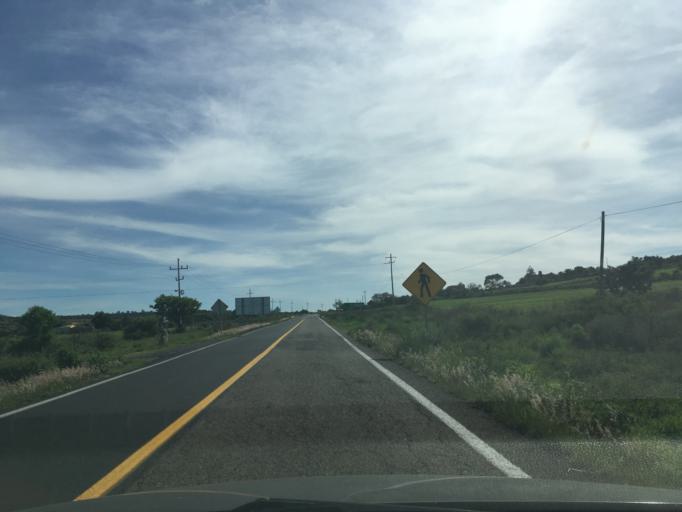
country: MX
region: Guanajuato
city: Coroneo
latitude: 20.1913
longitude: -100.4099
